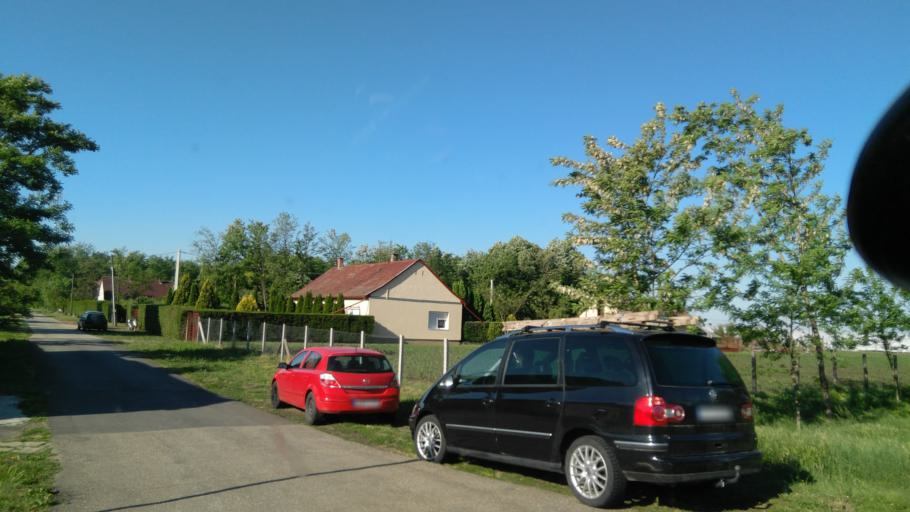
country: HU
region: Bekes
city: Elek
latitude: 46.5332
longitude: 21.2332
